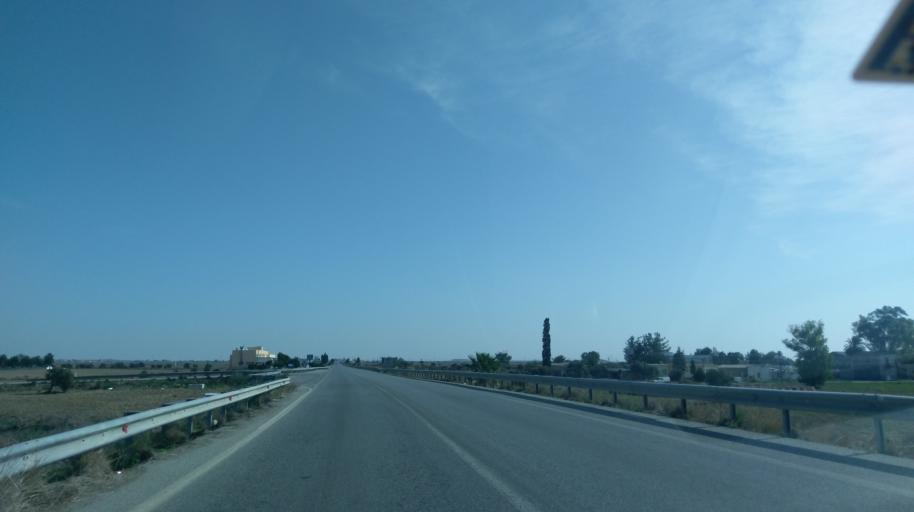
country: CY
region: Ammochostos
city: Lefkonoiko
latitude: 35.2569
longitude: 33.6843
